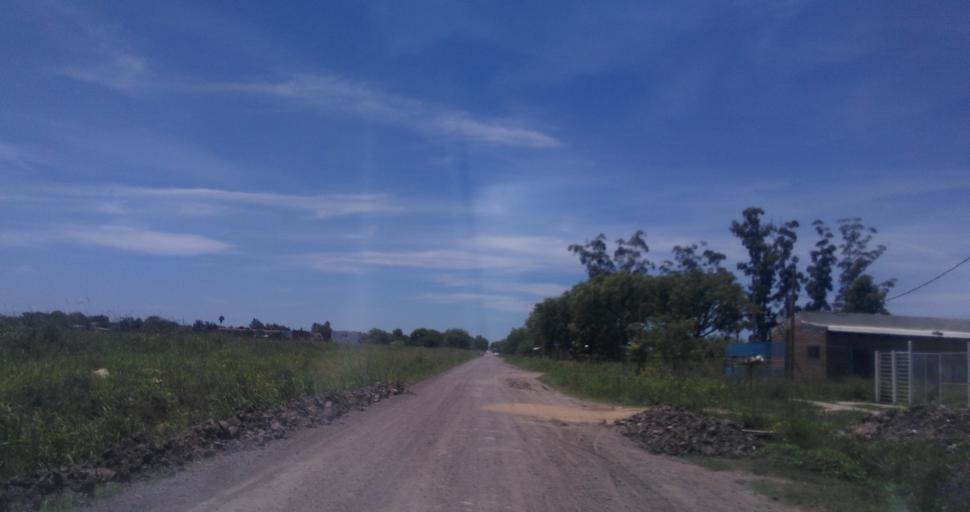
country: AR
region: Chaco
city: Fontana
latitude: -27.4232
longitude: -59.0432
